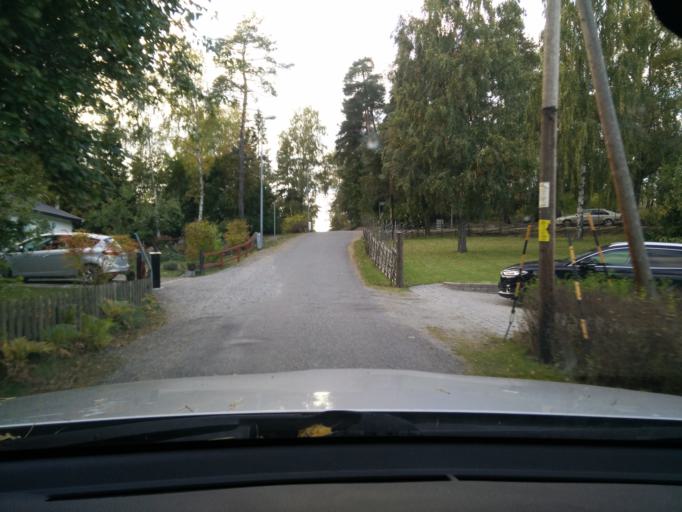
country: SE
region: Stockholm
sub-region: Stockholms Kommun
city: Kista
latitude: 59.4108
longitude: 17.9557
